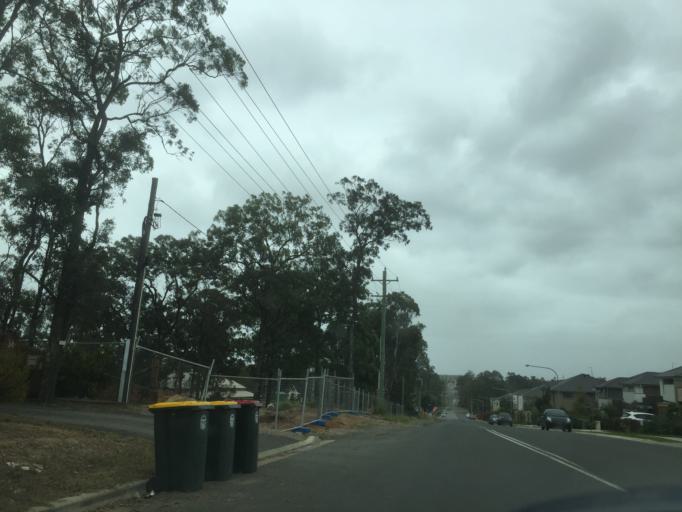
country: AU
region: New South Wales
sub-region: Blacktown
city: Stanhope Gardens
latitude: -33.7229
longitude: 150.9492
